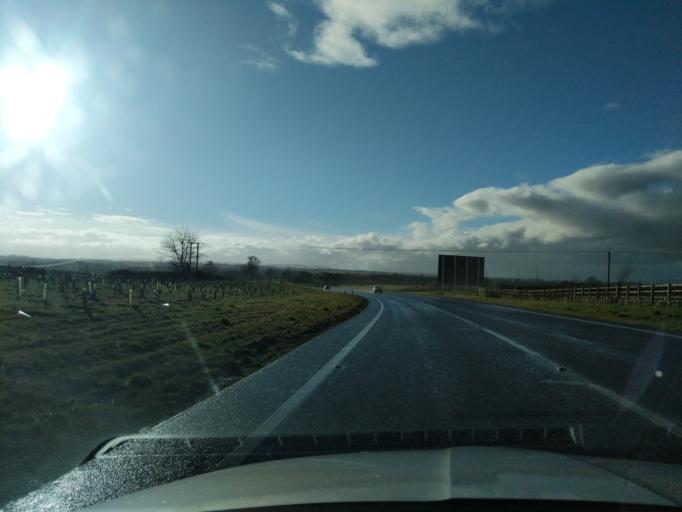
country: GB
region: England
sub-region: North Yorkshire
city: Bedale
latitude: 54.3096
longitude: -1.5751
